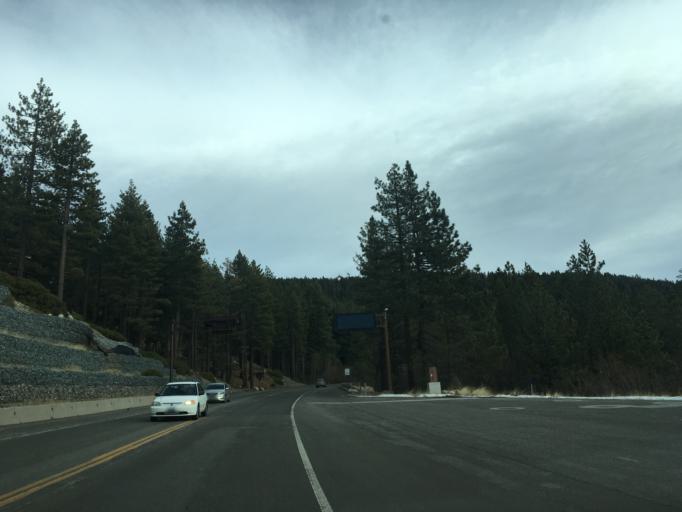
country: US
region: Nevada
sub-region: Washoe County
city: Incline Village
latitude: 39.2743
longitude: -119.9470
